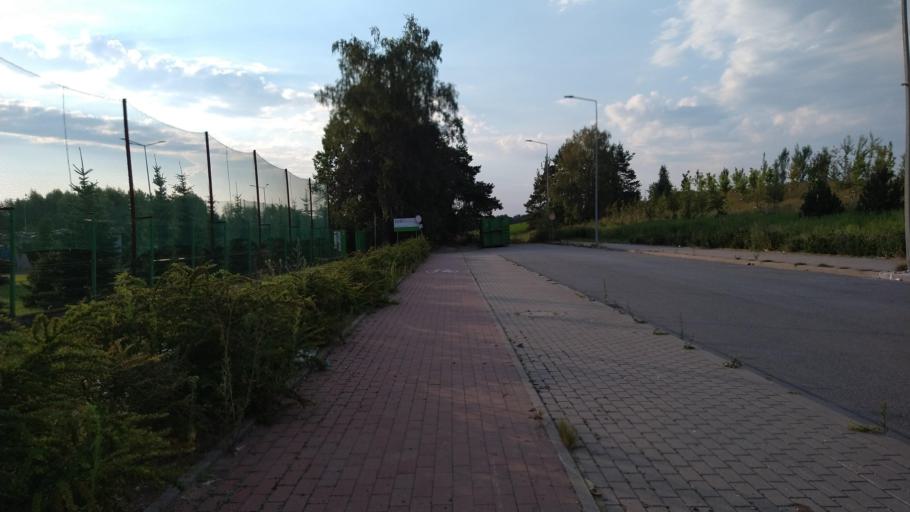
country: PL
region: Warmian-Masurian Voivodeship
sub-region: Powiat olsztynski
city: Olsztyn
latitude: 53.7885
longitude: 20.5533
